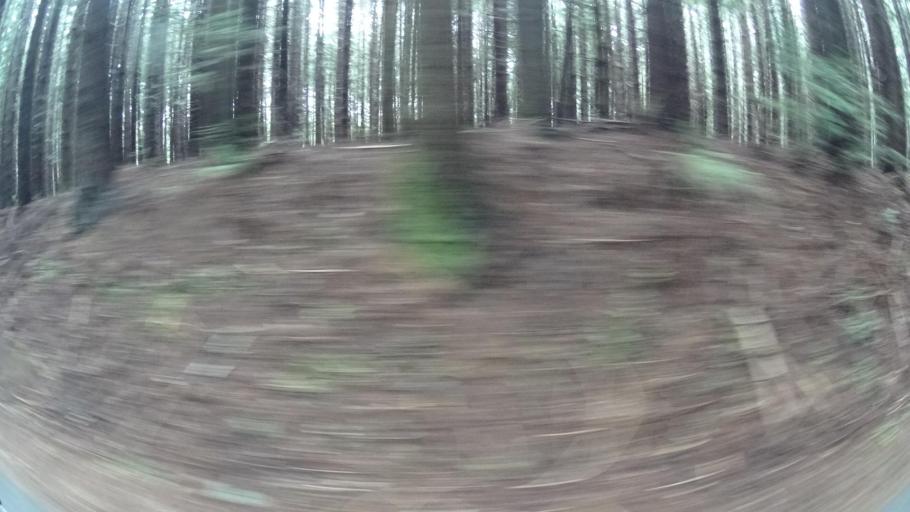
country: US
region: California
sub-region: Humboldt County
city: Westhaven-Moonstone
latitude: 41.2346
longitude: -123.9797
